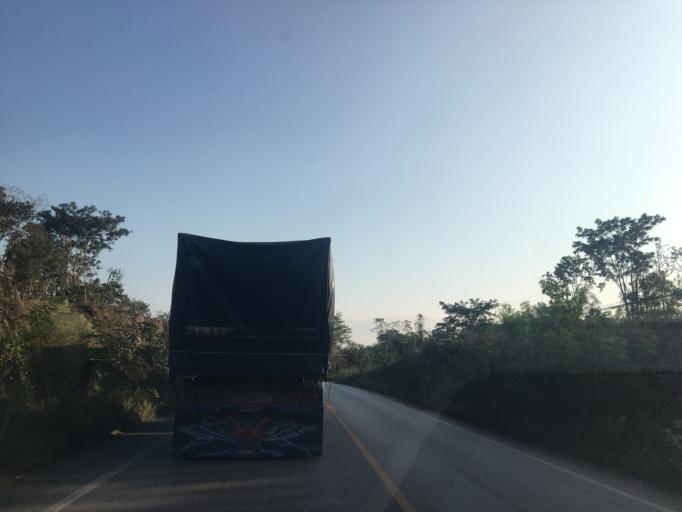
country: TH
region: Lampang
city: Ngao
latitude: 18.6605
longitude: 100.0176
